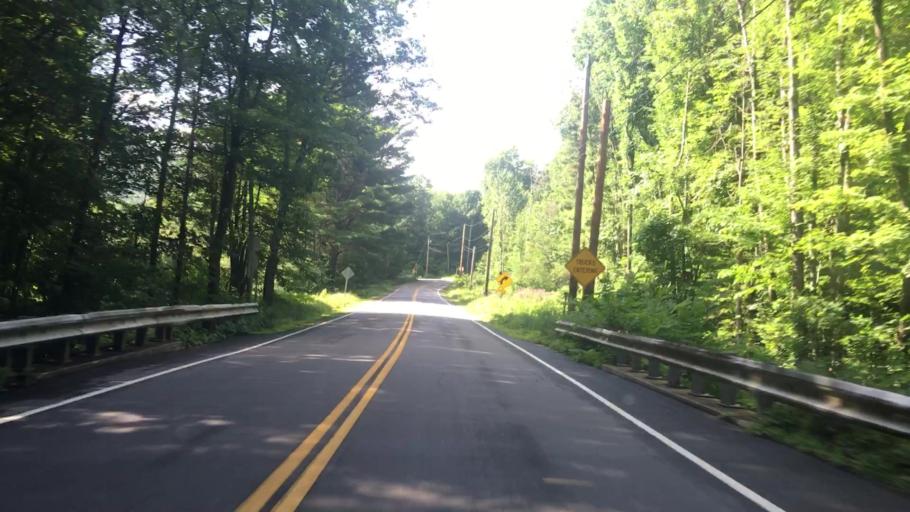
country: US
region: New Hampshire
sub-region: Belknap County
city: Gilford
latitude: 43.5359
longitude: -71.3221
